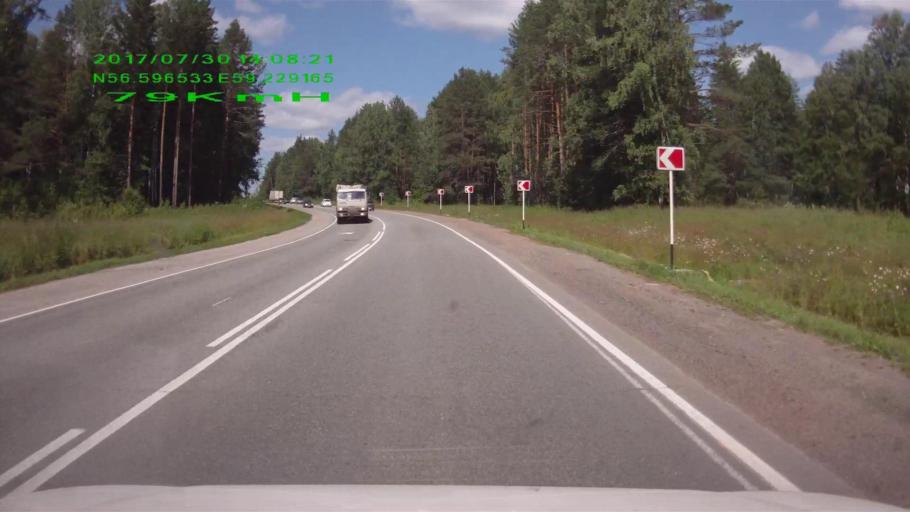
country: RU
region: Sverdlovsk
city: Nizhniye Sergi
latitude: 56.5972
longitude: 59.2295
